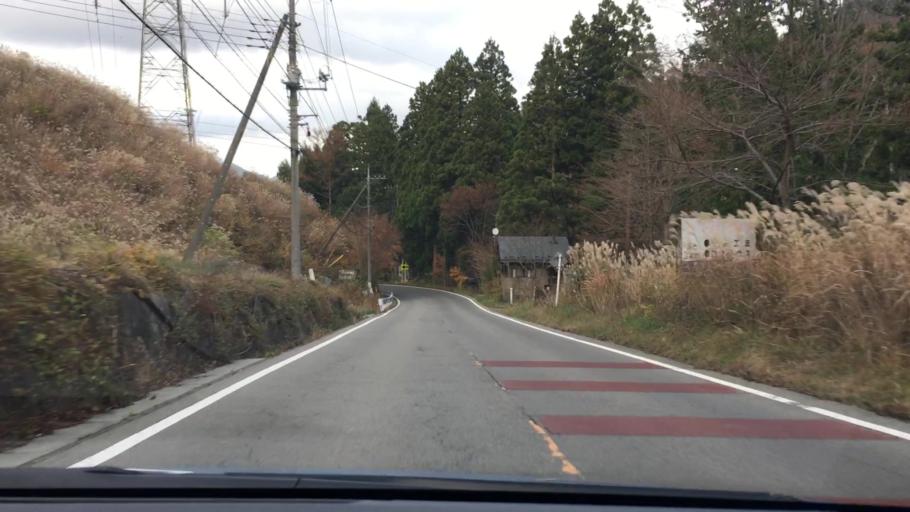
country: JP
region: Yamanashi
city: Otsuki
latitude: 35.4681
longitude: 138.9431
